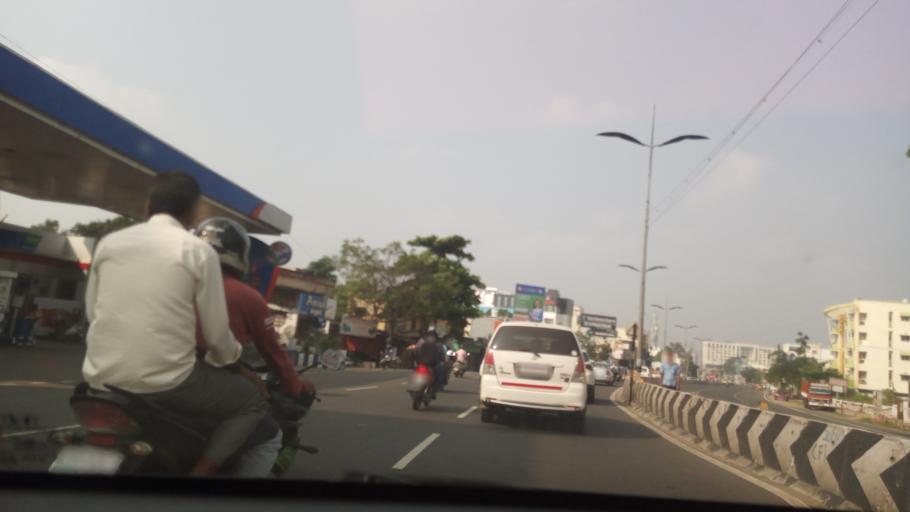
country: IN
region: Tamil Nadu
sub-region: Coimbatore
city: Coimbatore
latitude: 11.0225
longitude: 77.0002
